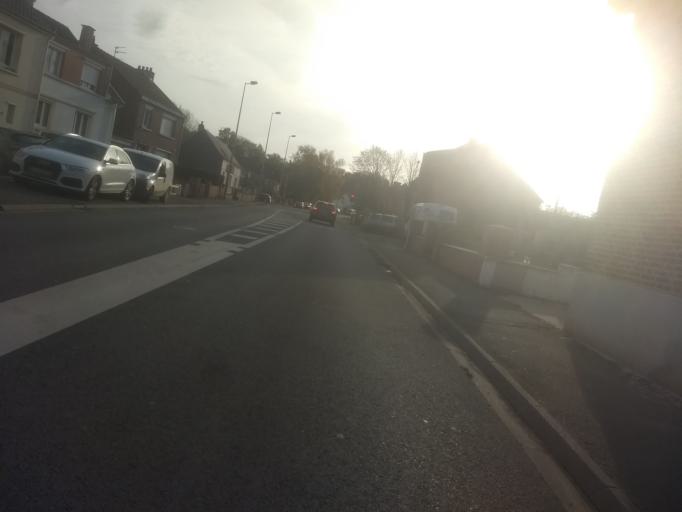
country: FR
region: Nord-Pas-de-Calais
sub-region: Departement du Pas-de-Calais
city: Achicourt
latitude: 50.2680
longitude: 2.7539
